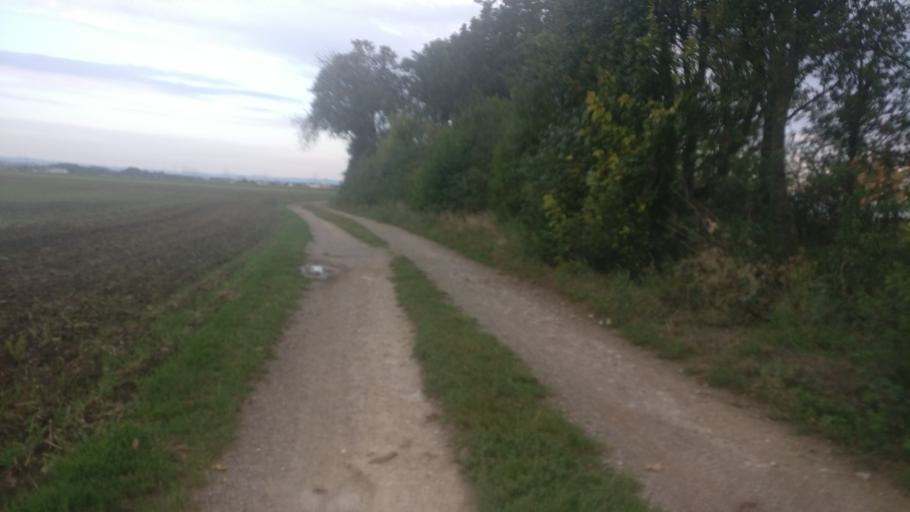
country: AT
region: Lower Austria
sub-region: Politischer Bezirk Wien-Umgebung
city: Lanzendorf
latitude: 48.1214
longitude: 16.4339
